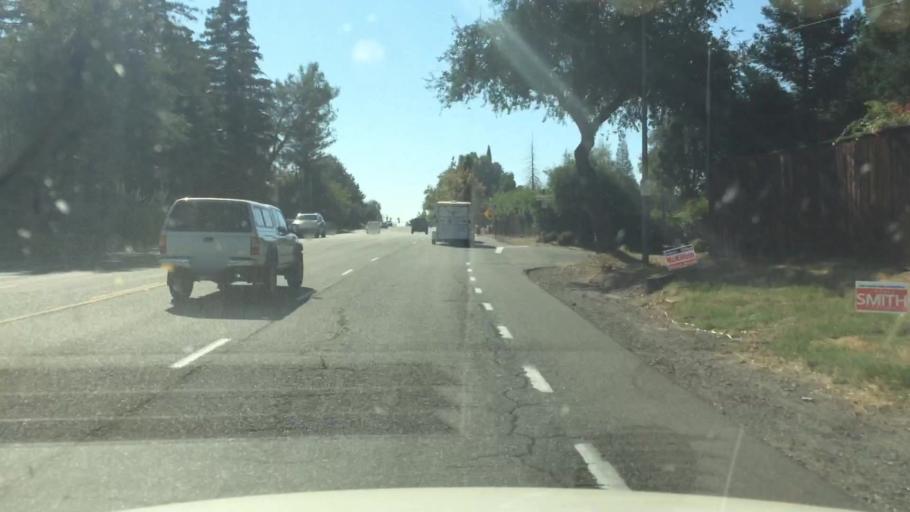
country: US
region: California
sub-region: Sacramento County
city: Orangevale
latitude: 38.6964
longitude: -121.2253
